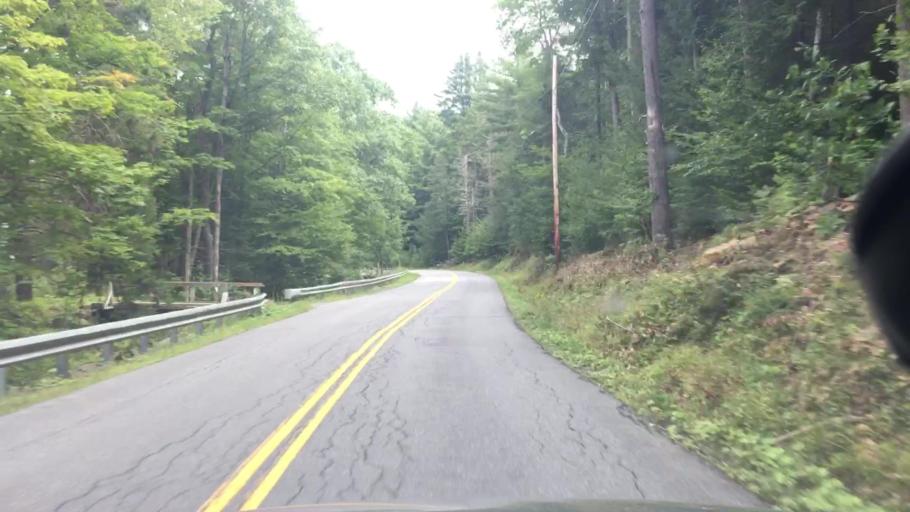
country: US
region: Vermont
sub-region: Windham County
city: Dover
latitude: 42.8045
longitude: -72.7681
